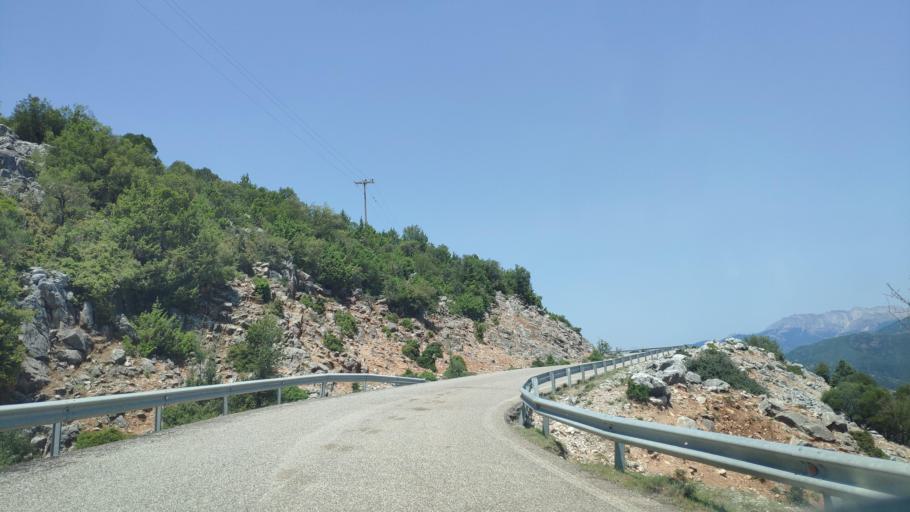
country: GR
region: Thessaly
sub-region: Nomos Kardhitsas
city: Anthiro
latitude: 39.1289
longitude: 21.3955
